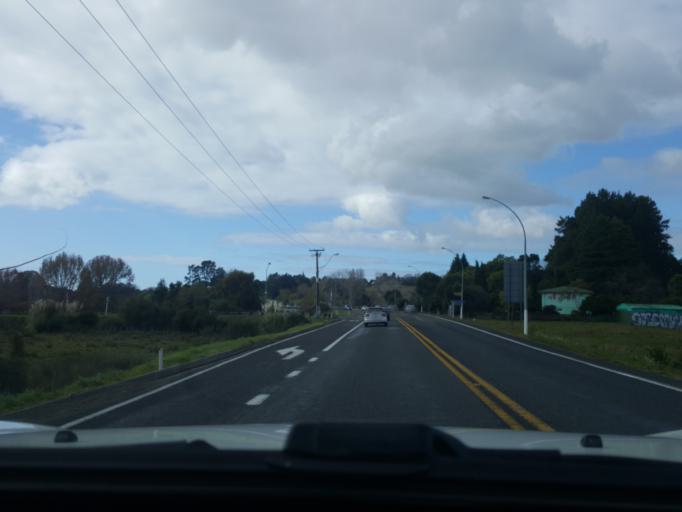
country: NZ
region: Bay of Plenty
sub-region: Tauranga City
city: Tauranga
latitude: -37.7002
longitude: 176.0910
